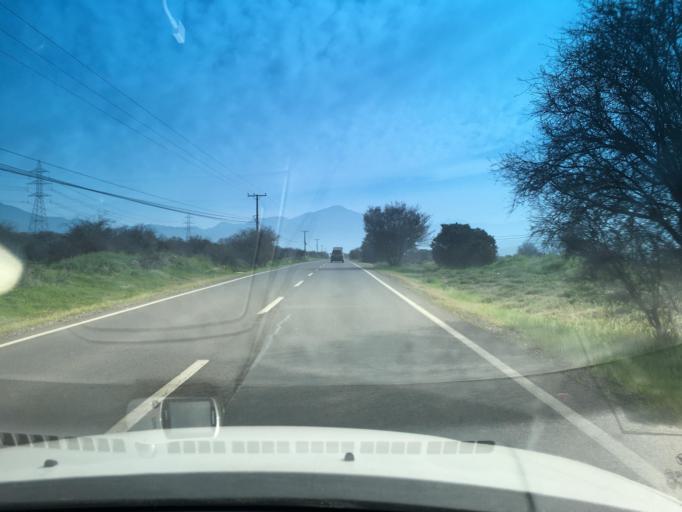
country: CL
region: Santiago Metropolitan
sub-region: Provincia de Chacabuco
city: Lampa
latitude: -33.1369
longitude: -70.9182
